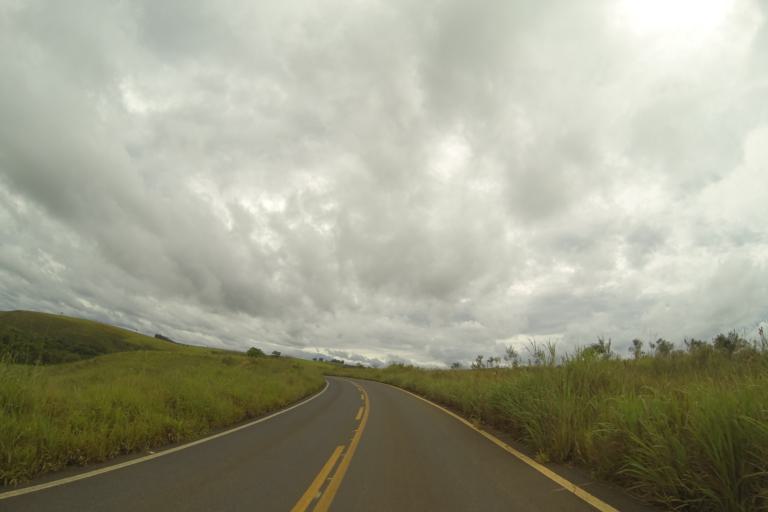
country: BR
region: Minas Gerais
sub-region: Bambui
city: Bambui
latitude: -20.0464
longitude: -46.1626
